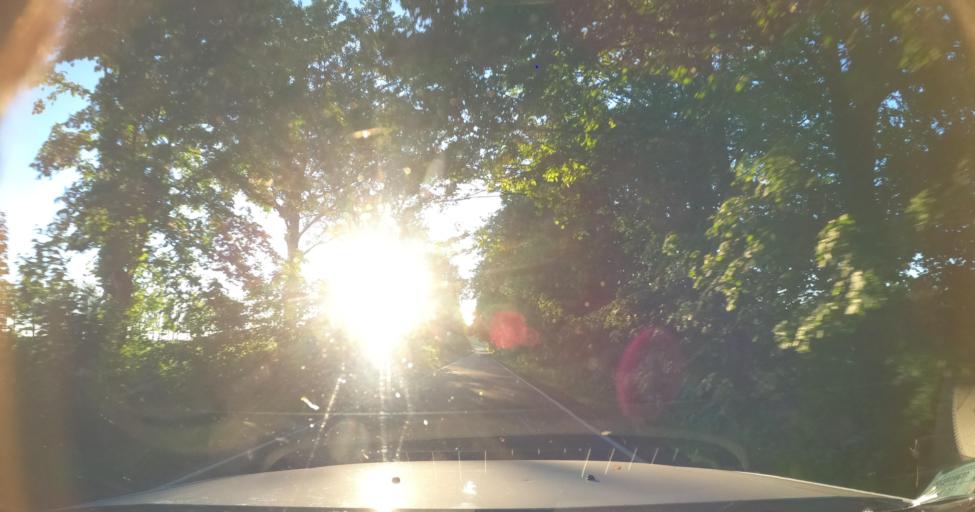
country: PL
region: Pomeranian Voivodeship
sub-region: Powiat slupski
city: Potegowo
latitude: 54.4111
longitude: 17.4190
